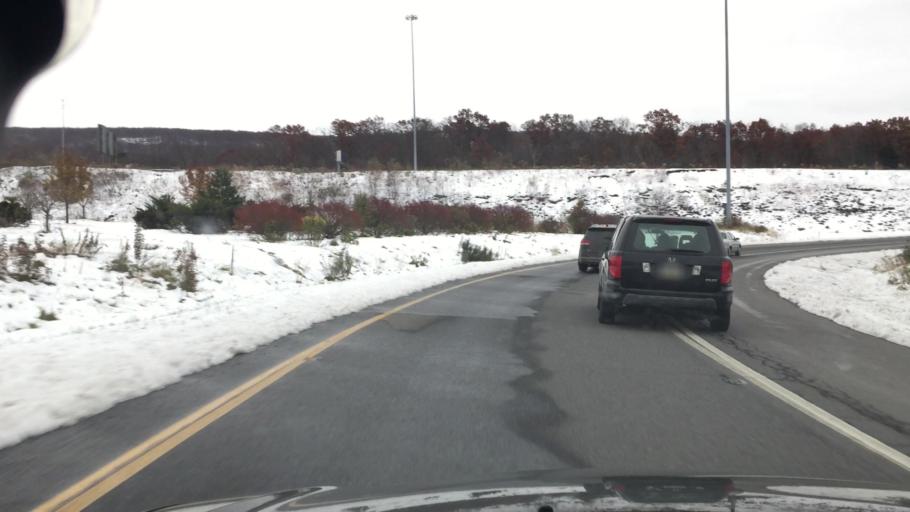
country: US
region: Pennsylvania
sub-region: Luzerne County
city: Georgetown
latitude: 41.2358
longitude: -75.8493
